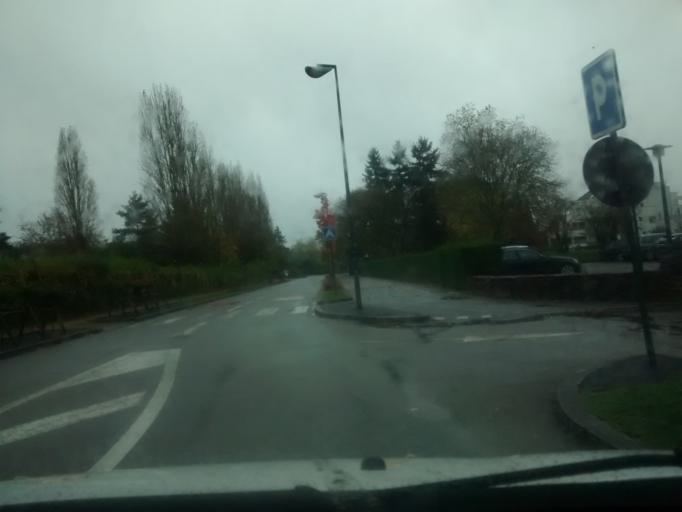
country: FR
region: Brittany
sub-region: Departement d'Ille-et-Vilaine
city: Chantepie
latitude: 48.0924
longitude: -1.6134
